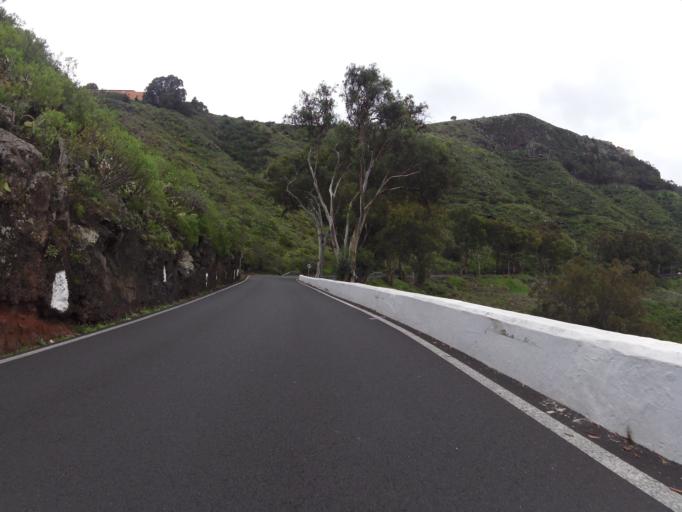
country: ES
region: Canary Islands
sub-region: Provincia de Las Palmas
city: Arucas
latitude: 28.0854
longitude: -15.5106
